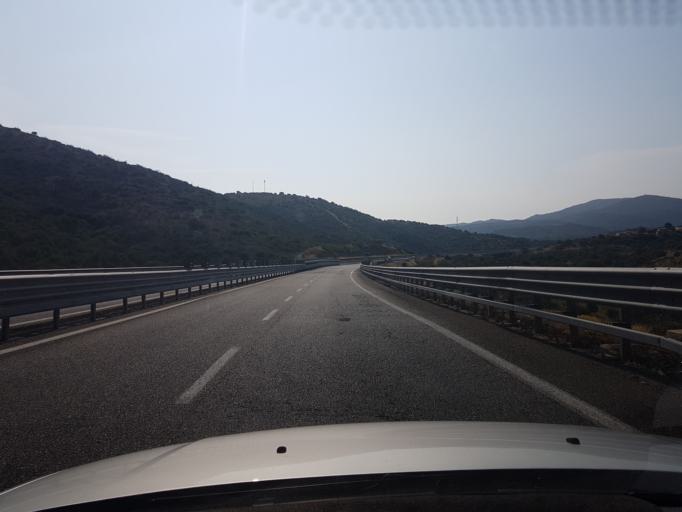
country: IT
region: Sardinia
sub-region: Provincia di Olbia-Tempio
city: San Teodoro
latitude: 40.7719
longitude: 9.6324
